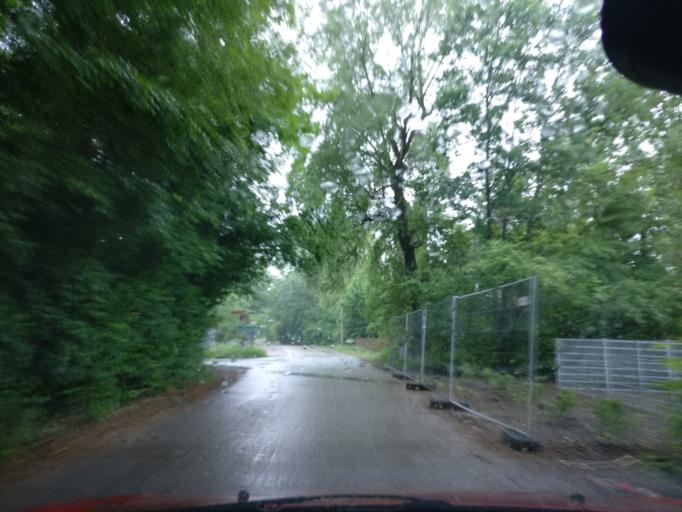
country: DE
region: Bavaria
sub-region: Upper Bavaria
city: Dachau
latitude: 48.2470
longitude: 11.4596
